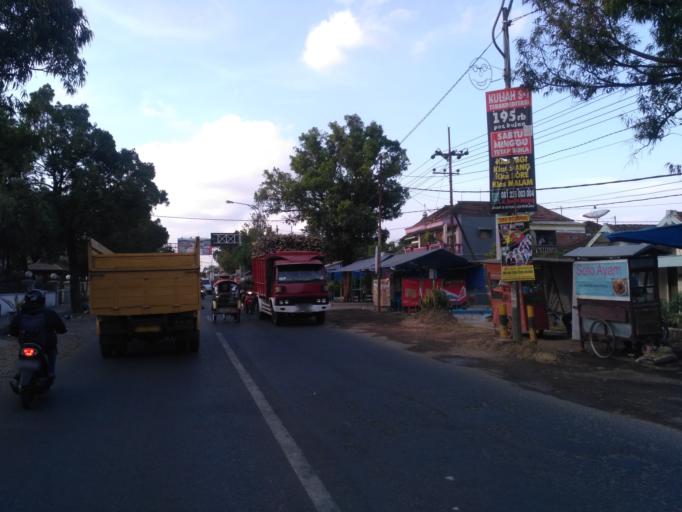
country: ID
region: East Java
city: Kebonsari
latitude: -8.0272
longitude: 112.6160
